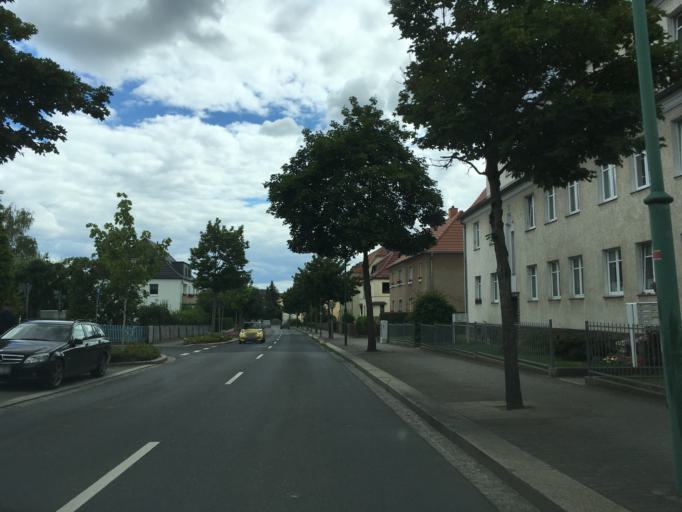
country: DE
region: Saxony
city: Radeberg
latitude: 51.1257
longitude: 13.9163
